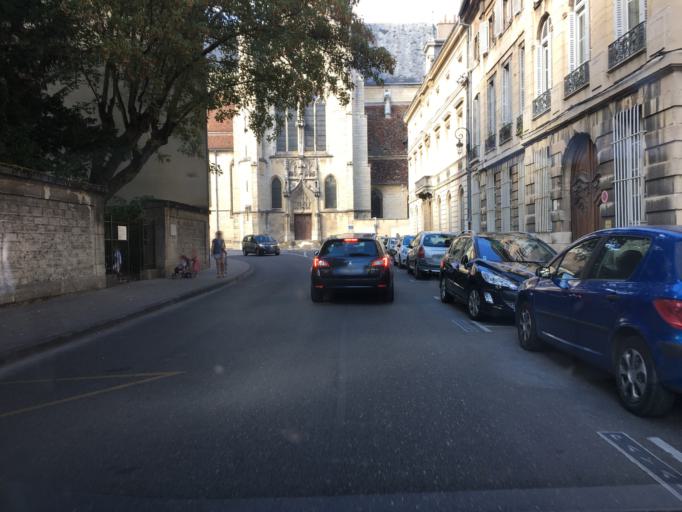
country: FR
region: Bourgogne
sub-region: Departement de la Cote-d'Or
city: Dijon
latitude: 47.3203
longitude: 5.0453
